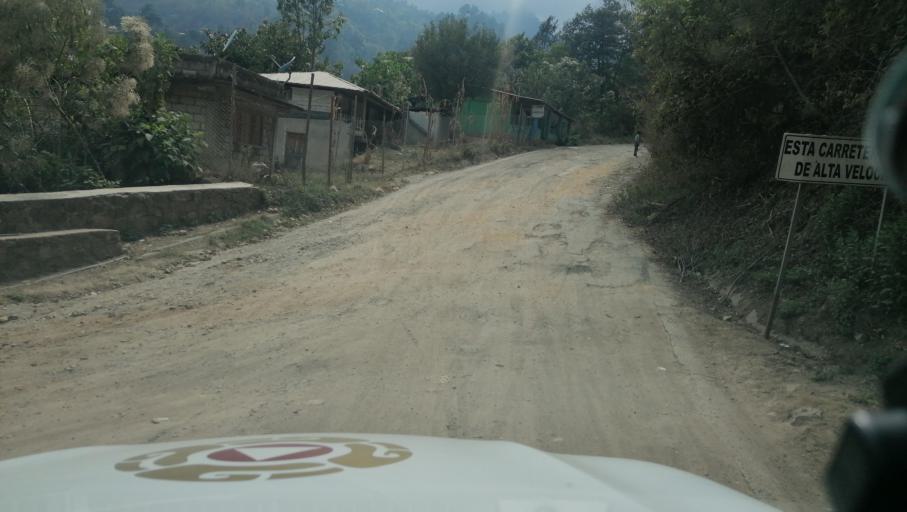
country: GT
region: San Marcos
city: Tacana
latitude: 15.2140
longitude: -92.1994
